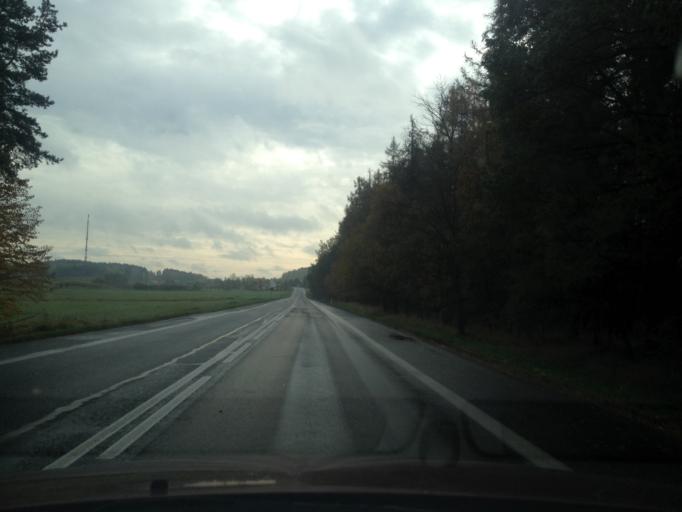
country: PL
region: Lower Silesian Voivodeship
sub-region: Powiat lubanski
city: Siekierczyn
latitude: 51.1561
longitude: 15.1544
